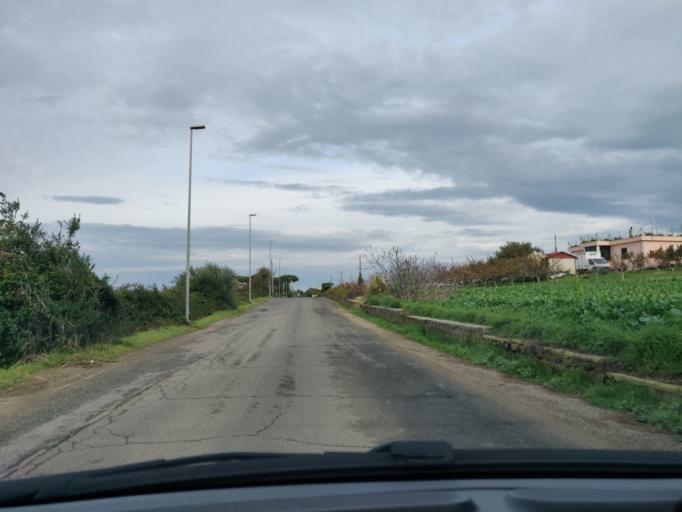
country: IT
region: Latium
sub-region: Citta metropolitana di Roma Capitale
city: Civitavecchia
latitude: 42.1011
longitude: 11.8131
